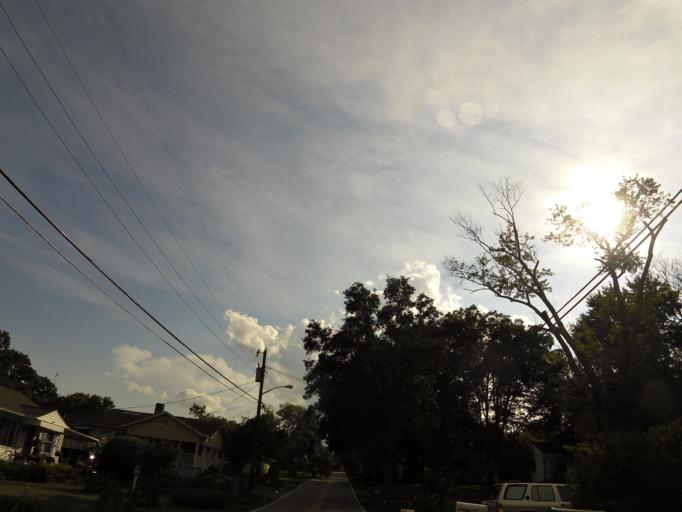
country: US
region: Tennessee
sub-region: Knox County
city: Knoxville
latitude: 36.0249
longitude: -83.9365
